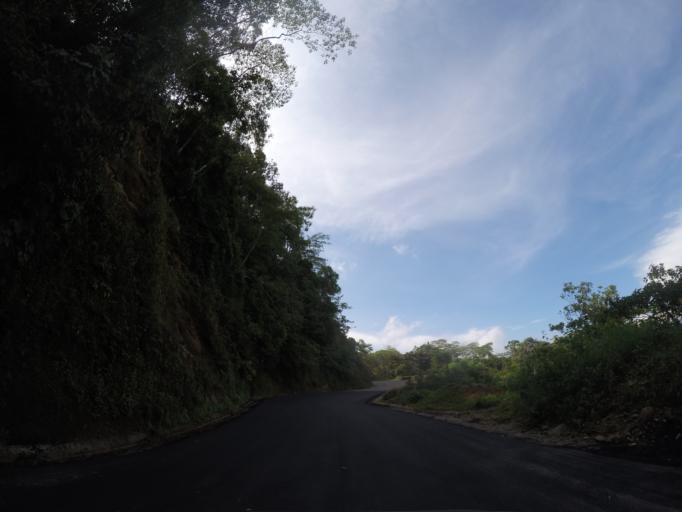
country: MX
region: Oaxaca
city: Pluma Hidalgo
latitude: 15.9347
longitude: -96.4310
